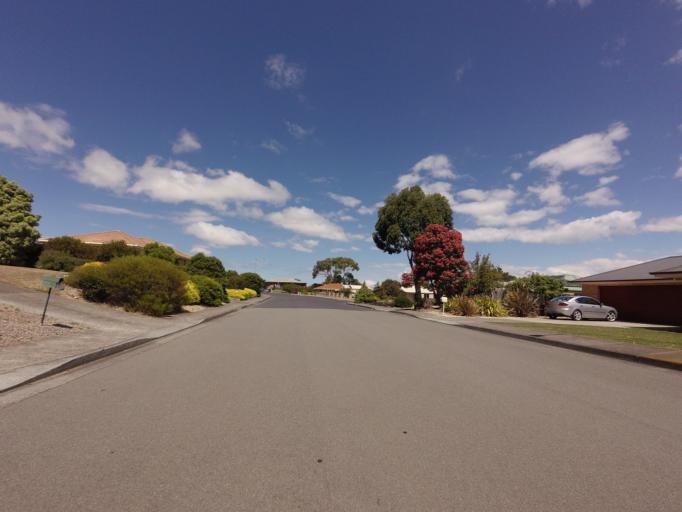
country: AU
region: Tasmania
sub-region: Clarence
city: Rokeby
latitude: -42.8989
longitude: 147.4565
